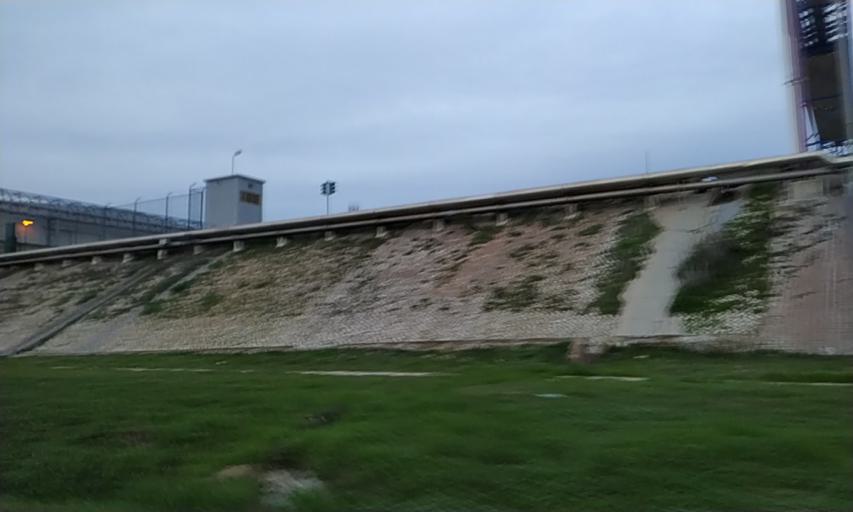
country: PT
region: Setubal
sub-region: Setubal
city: Setubal
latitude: 38.4992
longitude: -8.8390
